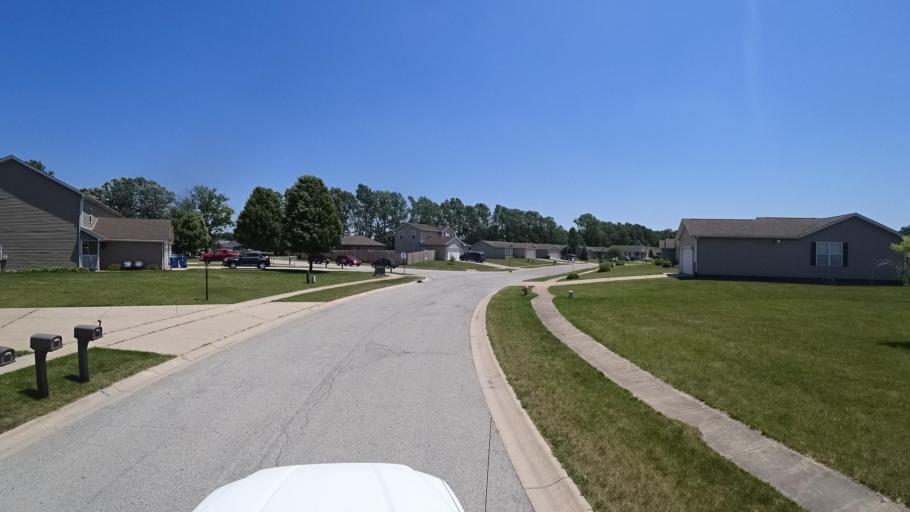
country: US
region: Indiana
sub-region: Porter County
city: Burns Harbor
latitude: 41.6042
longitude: -87.1359
